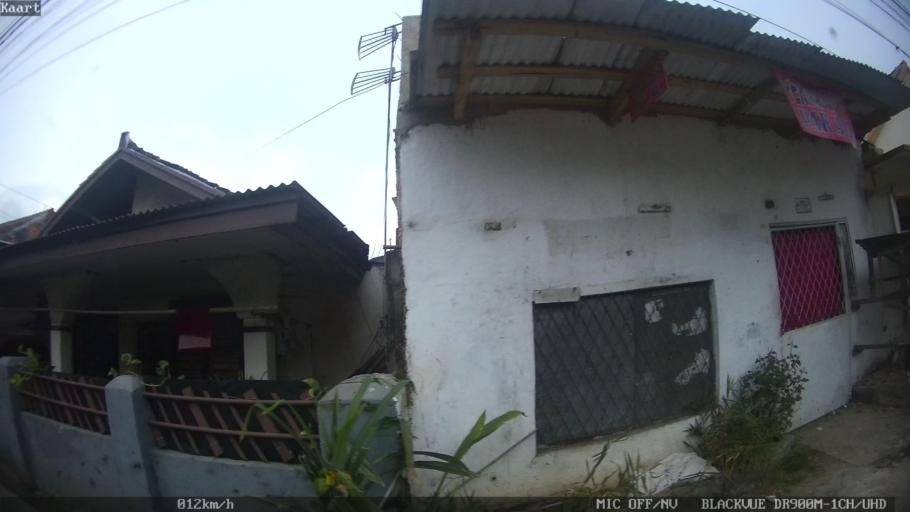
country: ID
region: Lampung
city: Kedaton
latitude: -5.4045
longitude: 105.2666
